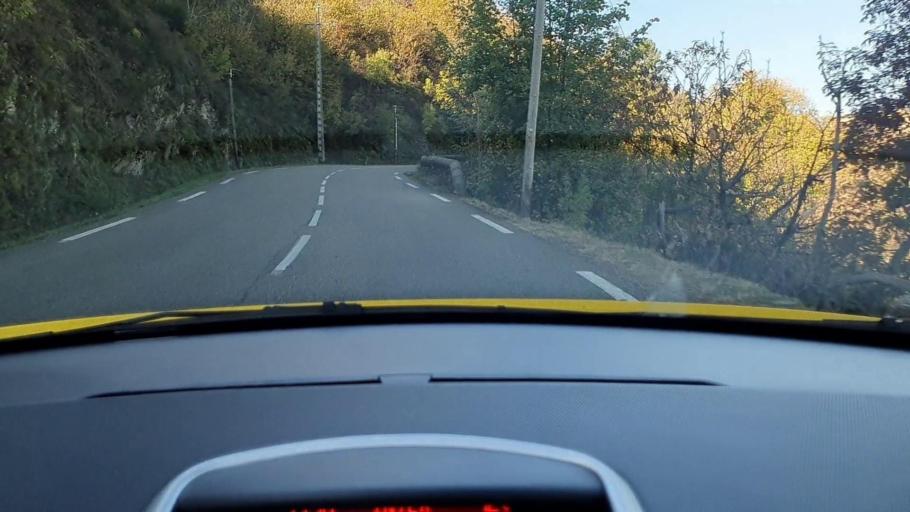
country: FR
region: Languedoc-Roussillon
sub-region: Departement du Gard
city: Sumene
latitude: 43.9854
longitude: 3.7049
